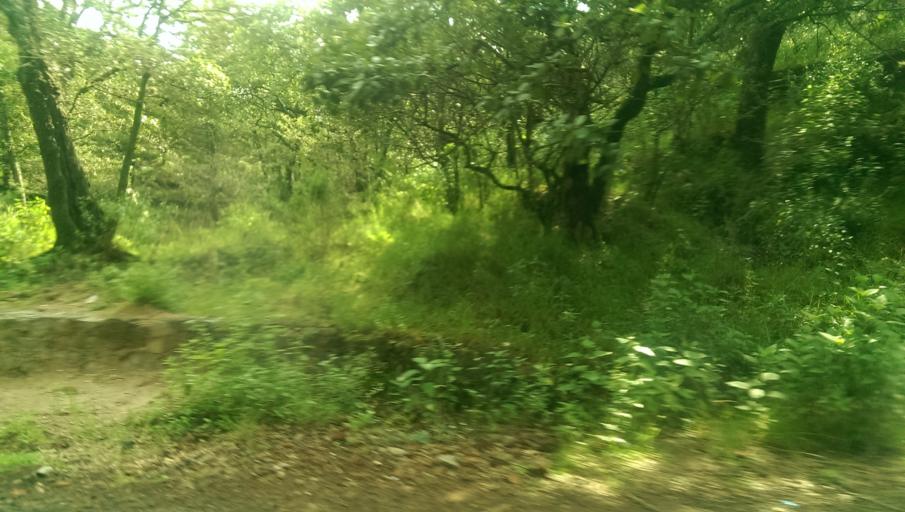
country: MX
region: Mexico
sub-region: Jilotepec
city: Jilotepec de Molina Enriquez
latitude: 19.9280
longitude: -99.4943
